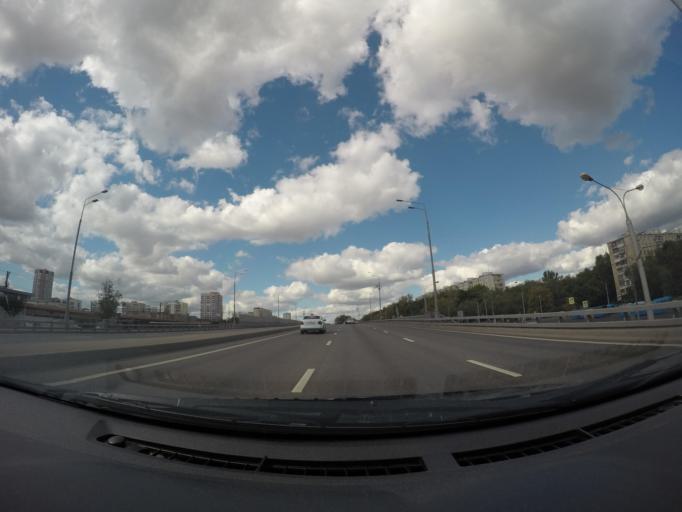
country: RU
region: Moscow
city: Veshnyaki
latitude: 55.7167
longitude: 37.8177
